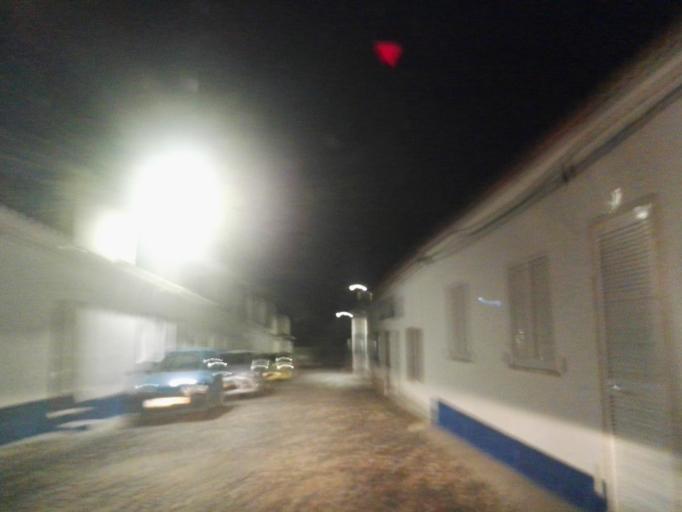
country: PT
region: Evora
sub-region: Montemor-O-Novo
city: Montemor-o-Novo
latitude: 38.5417
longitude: -8.1694
